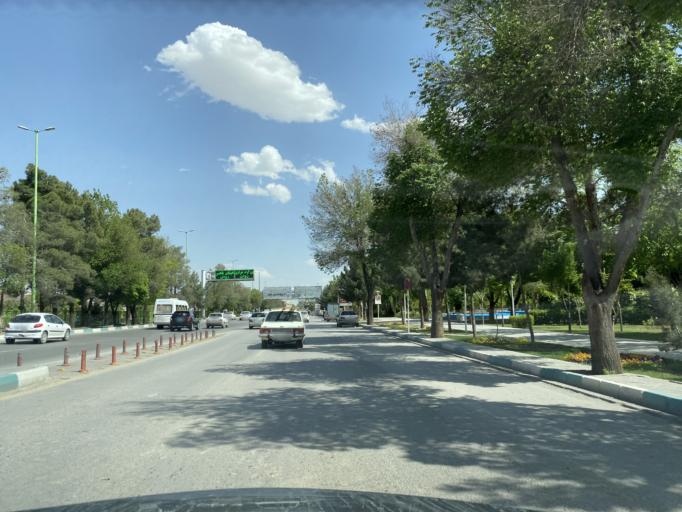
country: IR
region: Isfahan
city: Rehnan
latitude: 32.6839
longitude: 51.6382
